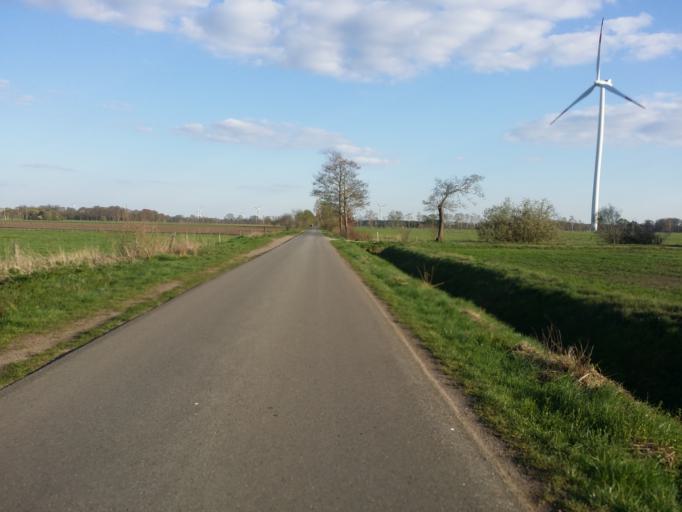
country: DE
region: Lower Saxony
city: Delmenhorst
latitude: 53.0141
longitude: 8.6280
